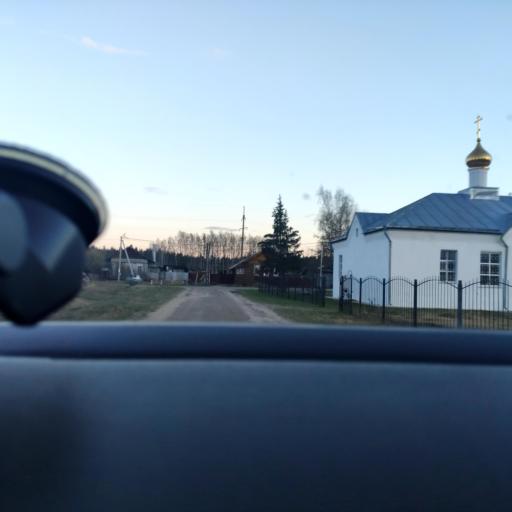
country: RU
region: Moskovskaya
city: Shaturtorf
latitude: 55.4341
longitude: 39.4275
